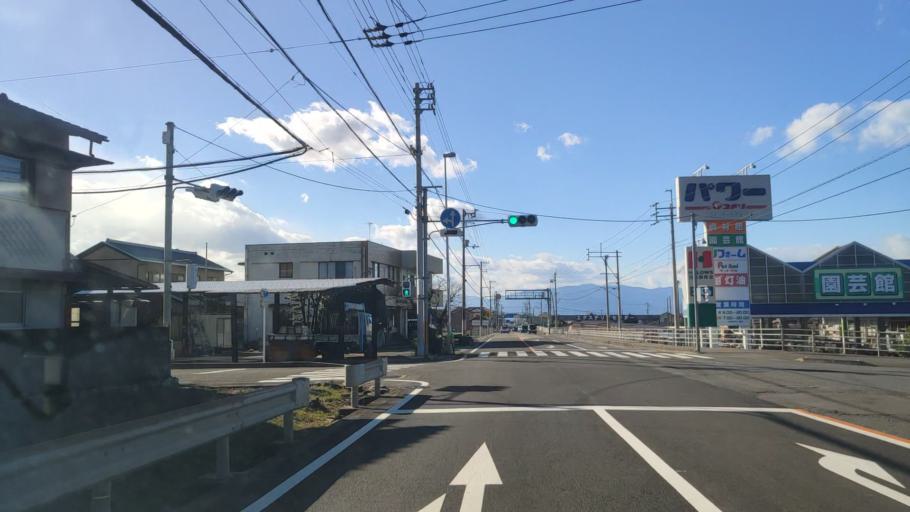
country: JP
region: Ehime
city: Saijo
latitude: 33.9191
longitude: 133.2300
